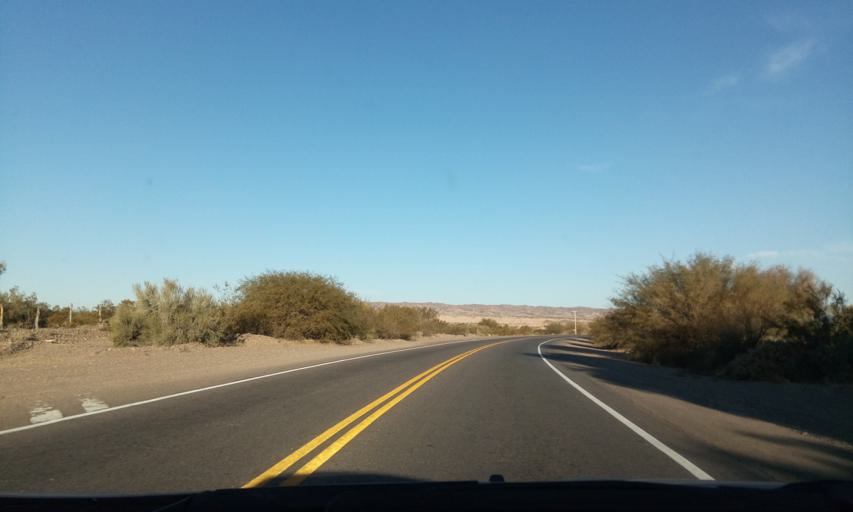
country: AR
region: San Juan
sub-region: Departamento de Rivadavia
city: Rivadavia
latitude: -31.4377
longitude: -68.6558
